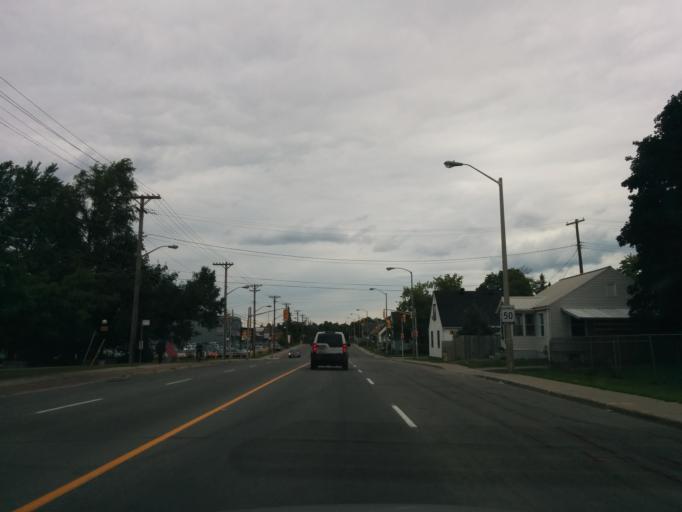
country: CA
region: Ontario
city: Ottawa
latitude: 45.3832
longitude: -75.7328
